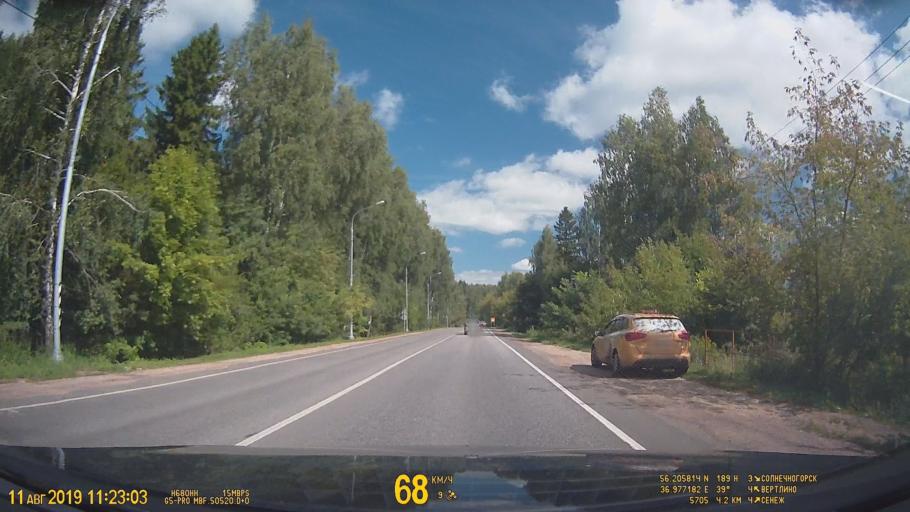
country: RU
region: Moskovskaya
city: Solnechnogorsk
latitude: 56.2061
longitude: 36.9775
